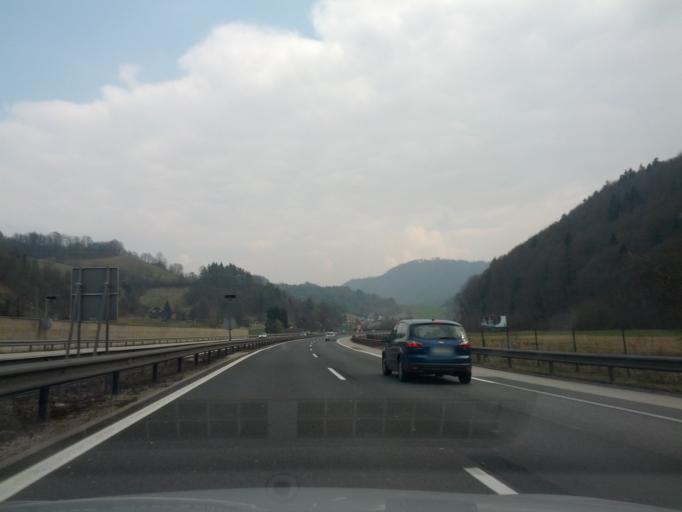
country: SI
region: Lukovica
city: Lukovica pri Domzalah
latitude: 46.1706
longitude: 14.7288
